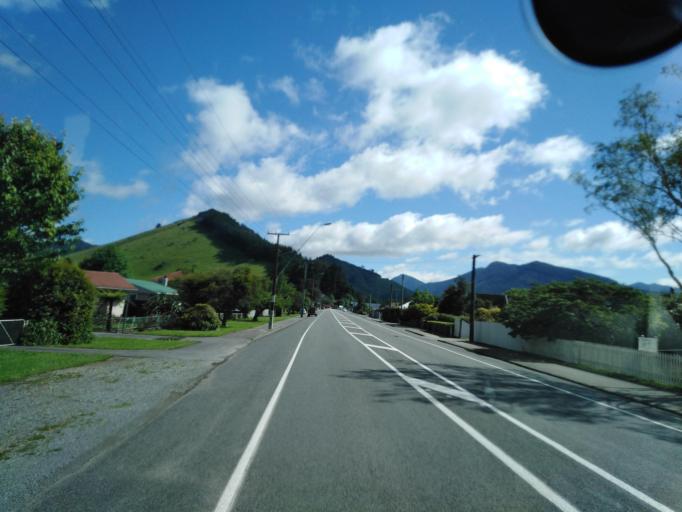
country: NZ
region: Nelson
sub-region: Nelson City
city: Nelson
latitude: -41.2308
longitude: 173.5821
